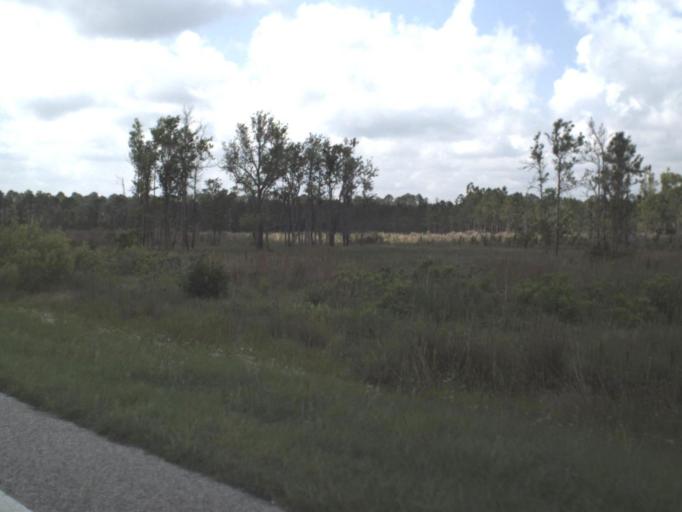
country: US
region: Florida
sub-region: Saint Johns County
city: Butler Beach
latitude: 29.6970
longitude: -81.2968
